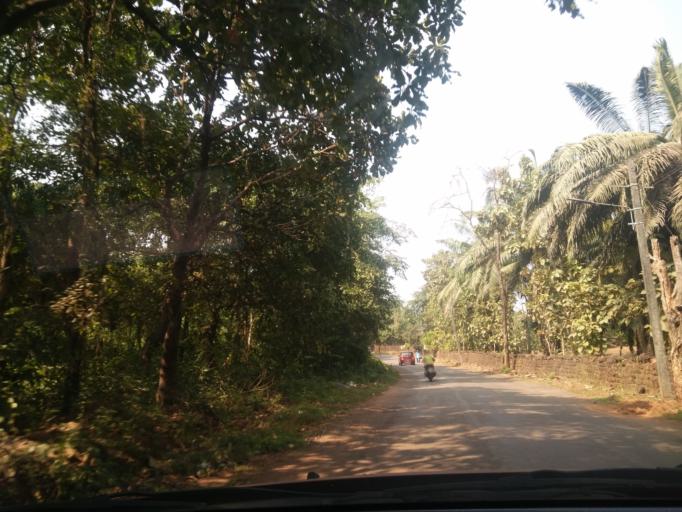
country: IN
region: Goa
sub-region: North Goa
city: Valpoy
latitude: 15.5091
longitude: 74.1313
